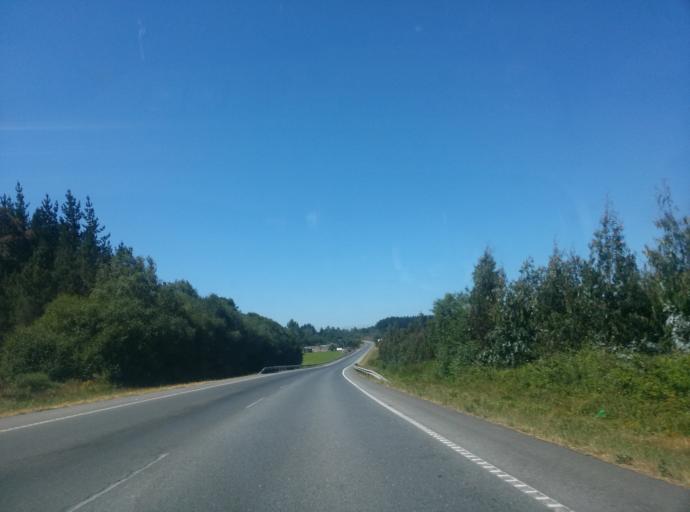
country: ES
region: Galicia
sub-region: Provincia de Lugo
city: Mos
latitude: 43.1171
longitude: -7.4853
